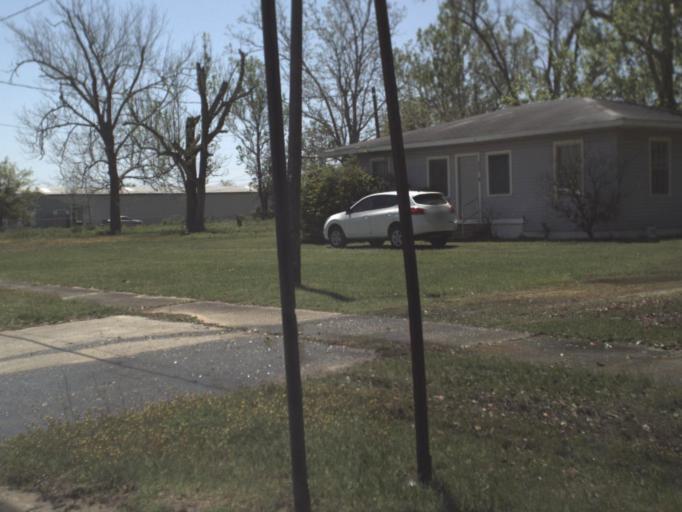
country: US
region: Florida
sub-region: Escambia County
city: Bellview
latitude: 30.4804
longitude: -87.3067
